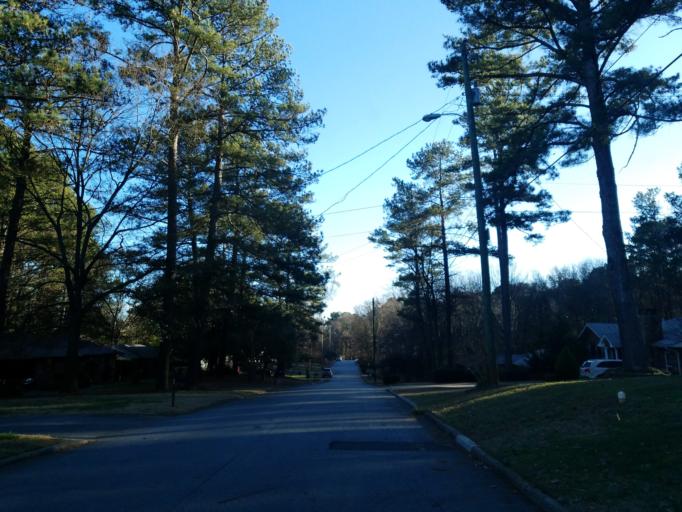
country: US
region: Georgia
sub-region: Cobb County
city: Fair Oaks
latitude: 33.9371
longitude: -84.4931
